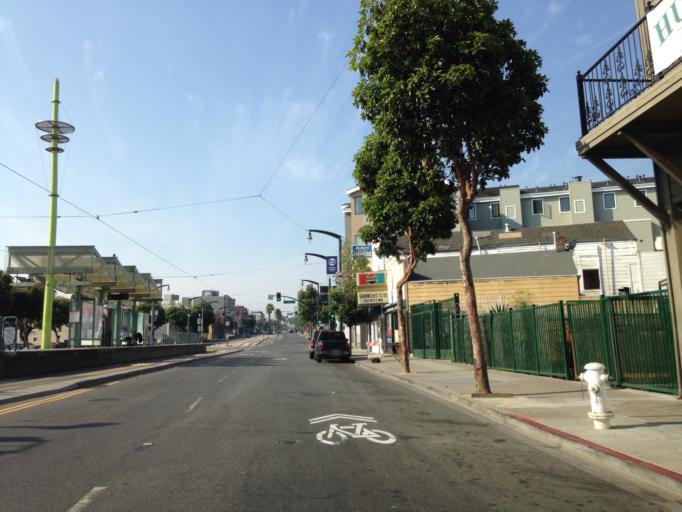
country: US
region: California
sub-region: San Francisco County
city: San Francisco
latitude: 37.7403
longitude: -122.3889
